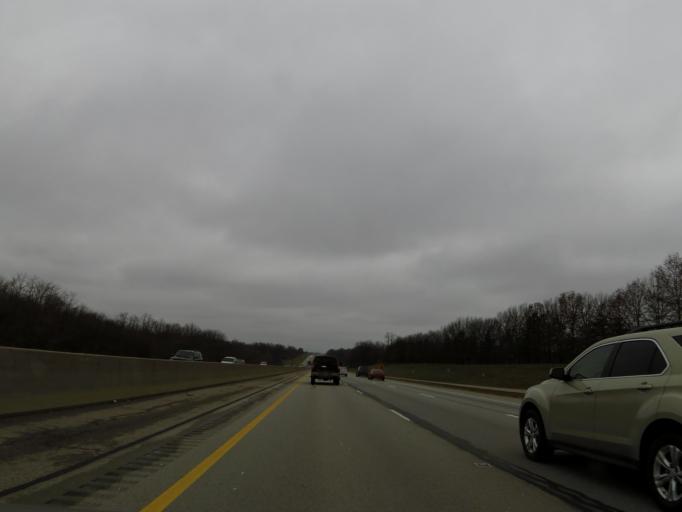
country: US
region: Kentucky
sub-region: Grant County
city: Crittenden
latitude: 38.8157
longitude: -84.6012
